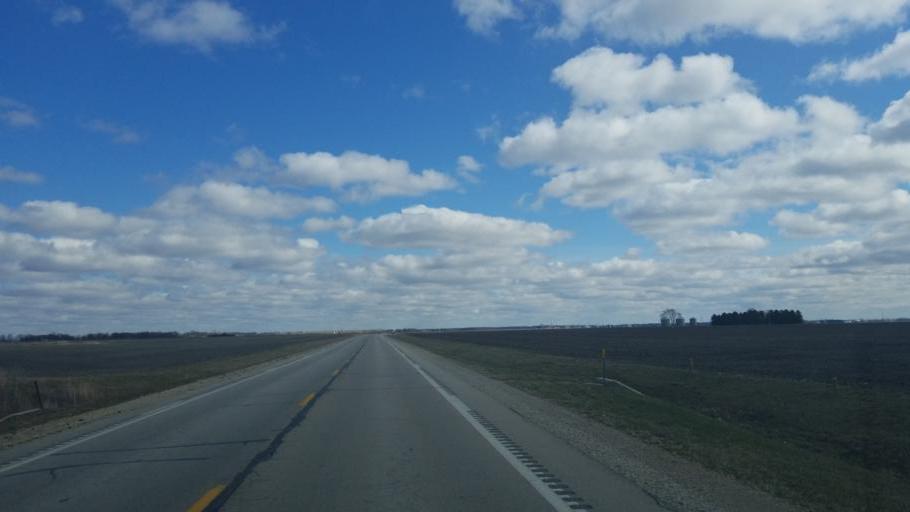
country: US
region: Illinois
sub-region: Douglas County
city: Villa Grove
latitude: 39.7919
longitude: -88.1088
